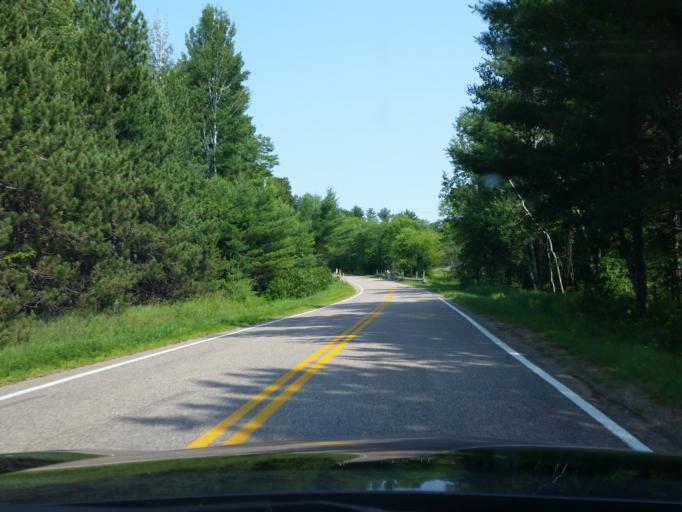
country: CA
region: Quebec
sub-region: Outaouais
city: Shawville
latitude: 45.5241
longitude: -76.4481
